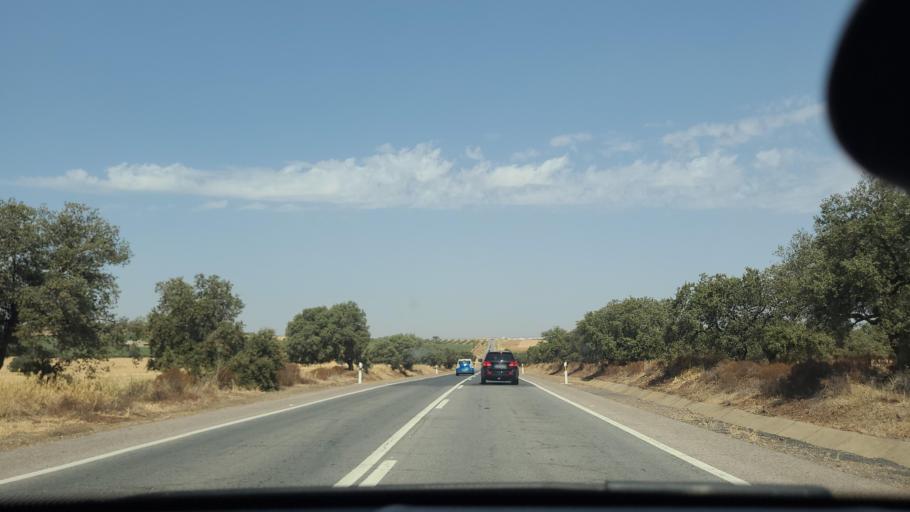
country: ES
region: Extremadura
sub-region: Provincia de Badajoz
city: Santa Marta
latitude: 38.5744
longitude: -6.5881
